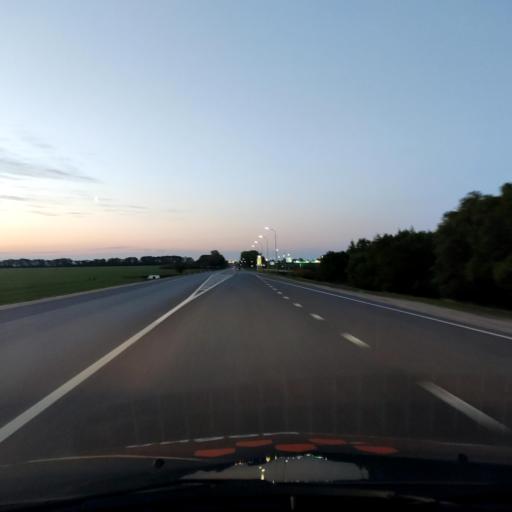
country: RU
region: Orjol
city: Zmiyevka
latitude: 52.7129
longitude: 36.3485
